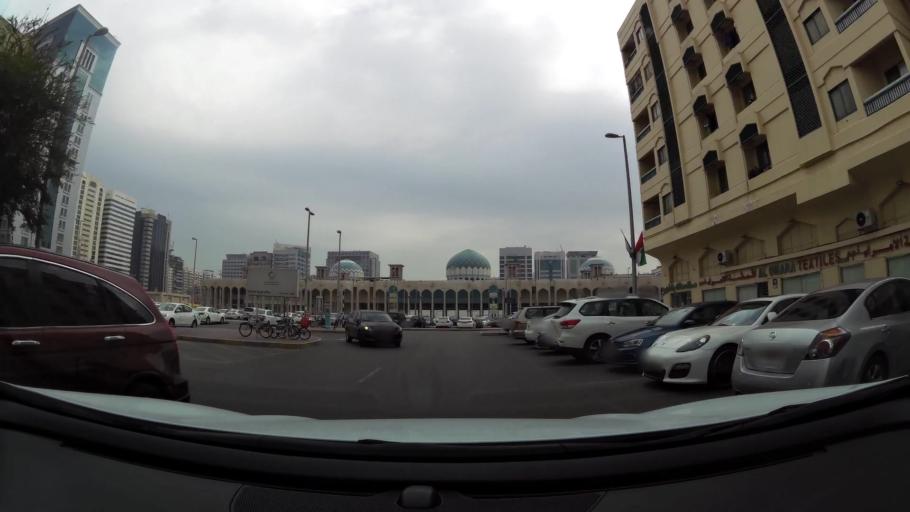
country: AE
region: Abu Dhabi
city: Abu Dhabi
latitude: 24.4829
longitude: 54.3639
